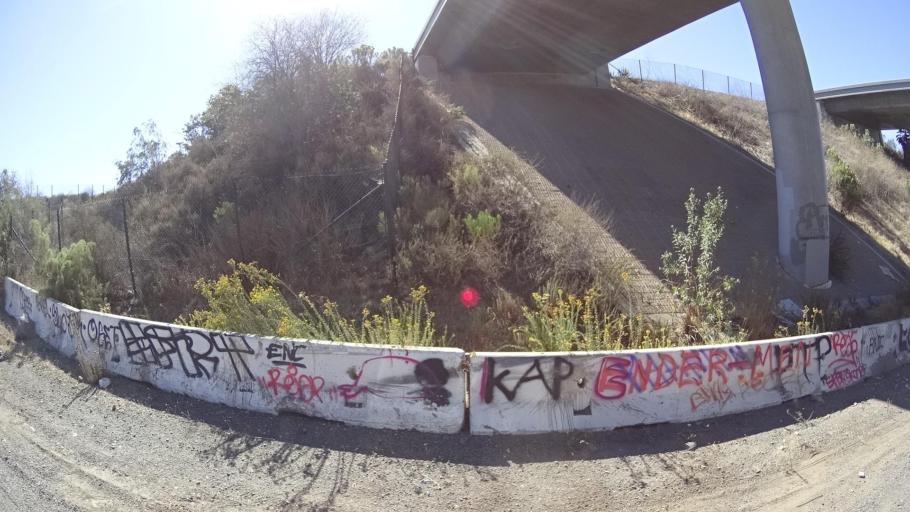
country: US
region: California
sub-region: San Diego County
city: La Presa
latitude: 32.6655
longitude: -116.9834
